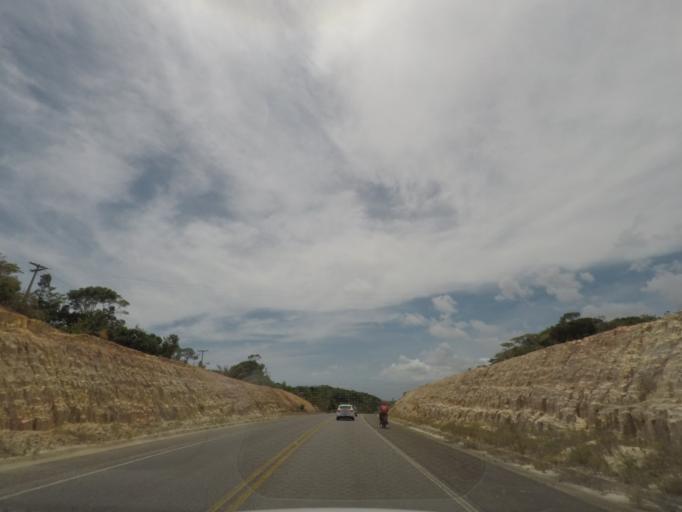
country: BR
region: Bahia
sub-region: Conde
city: Conde
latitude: -12.0211
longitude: -37.6917
